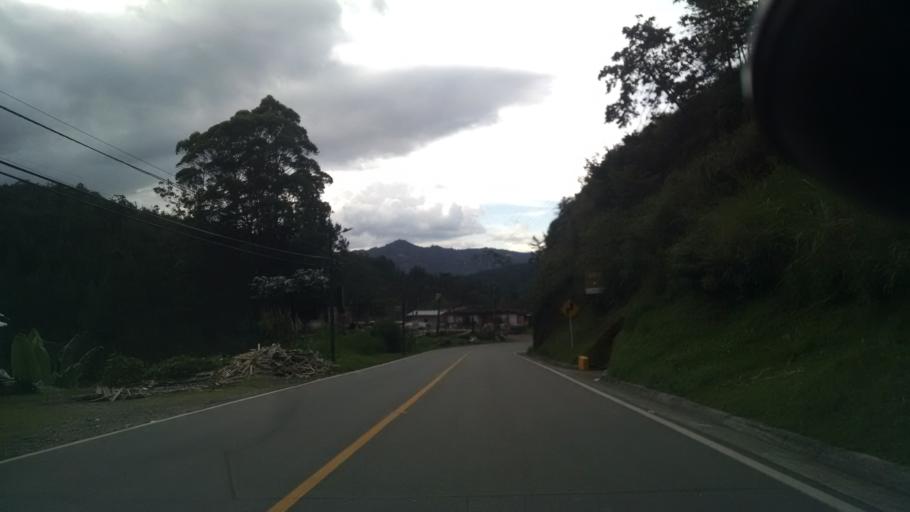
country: CO
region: Antioquia
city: El Retiro
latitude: 6.0835
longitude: -75.4771
